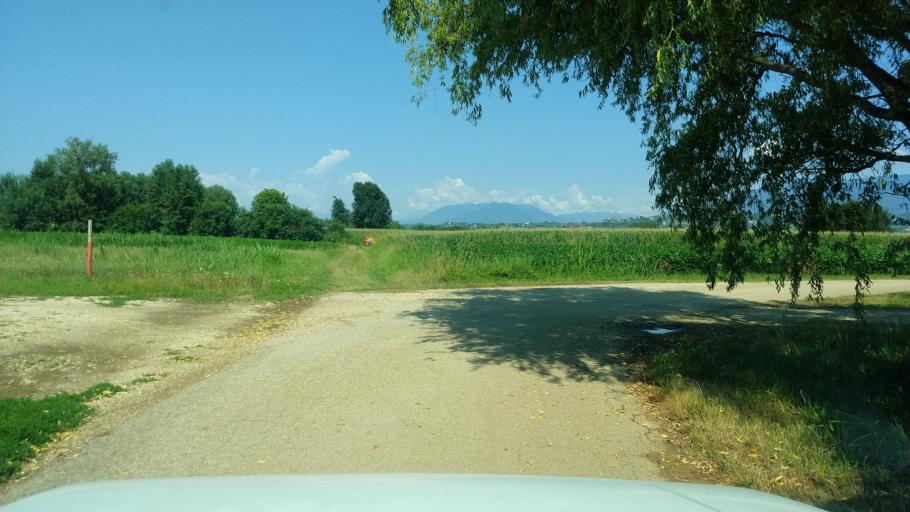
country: IT
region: Veneto
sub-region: Provincia di Vicenza
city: Schiavon
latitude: 45.7068
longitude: 11.6325
